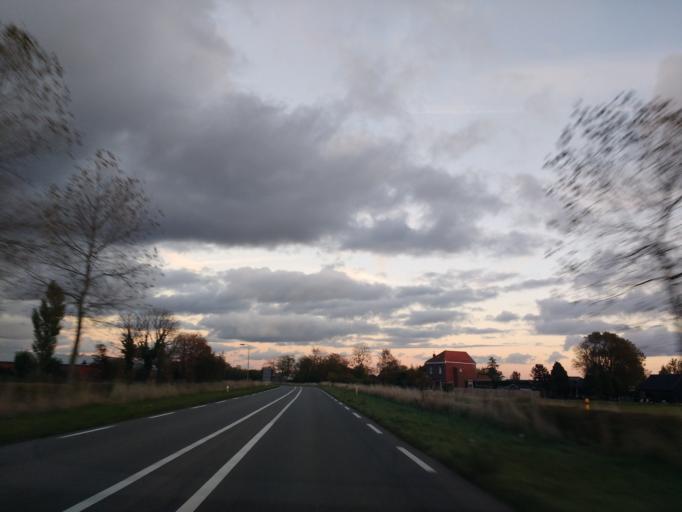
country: NL
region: Zeeland
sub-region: Gemeente Sluis
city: Sluis
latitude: 51.2993
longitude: 3.4228
